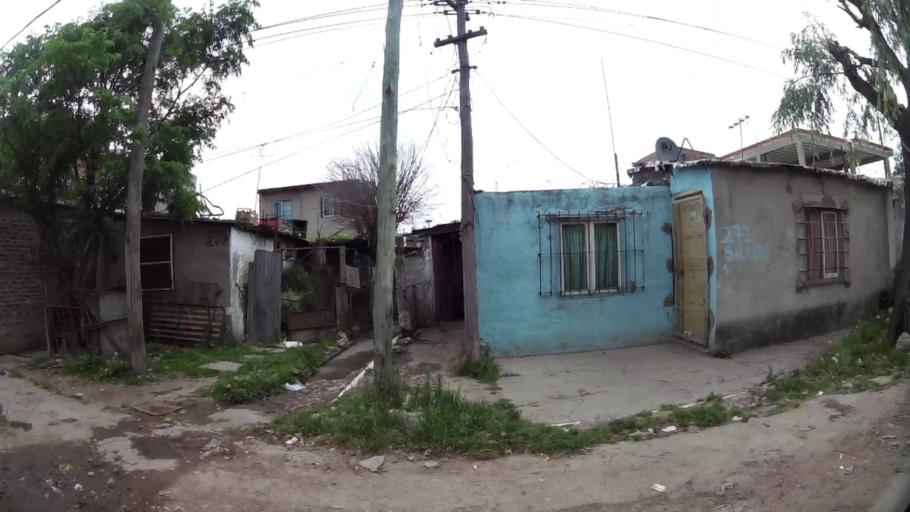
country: AR
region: Buenos Aires
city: San Justo
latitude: -34.6743
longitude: -58.5223
